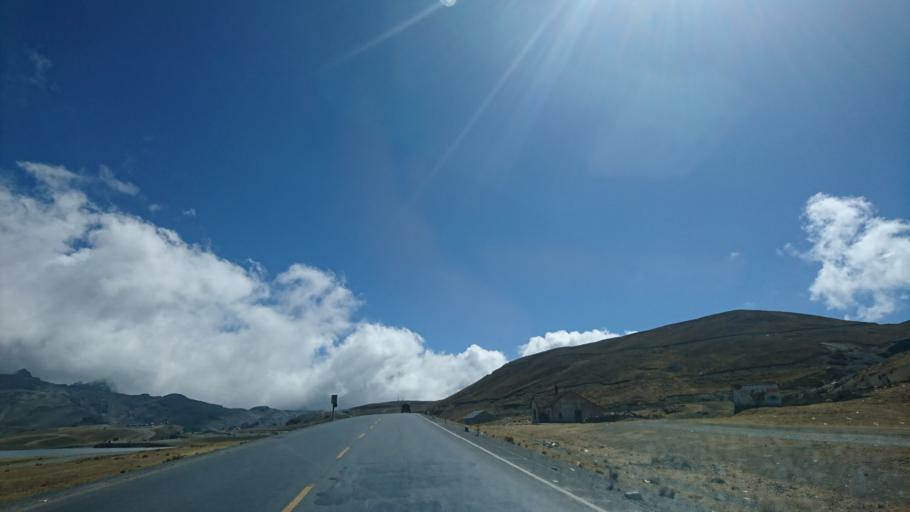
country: BO
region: La Paz
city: La Paz
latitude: -16.3453
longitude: -68.0395
